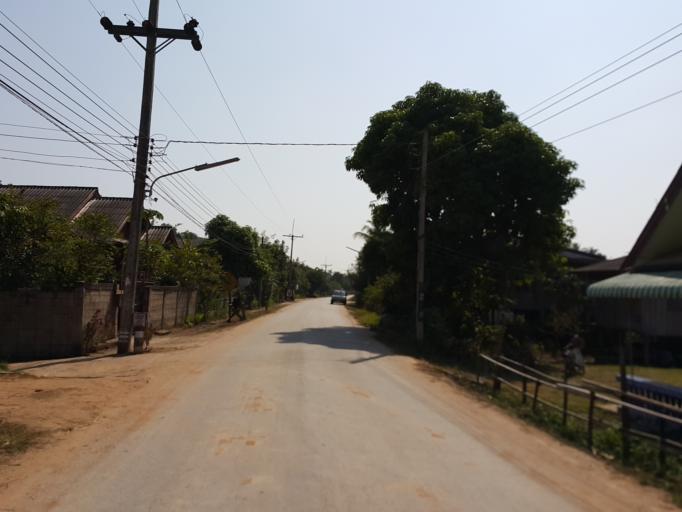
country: TH
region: Lampang
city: Wang Nuea
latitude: 19.0369
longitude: 99.6237
